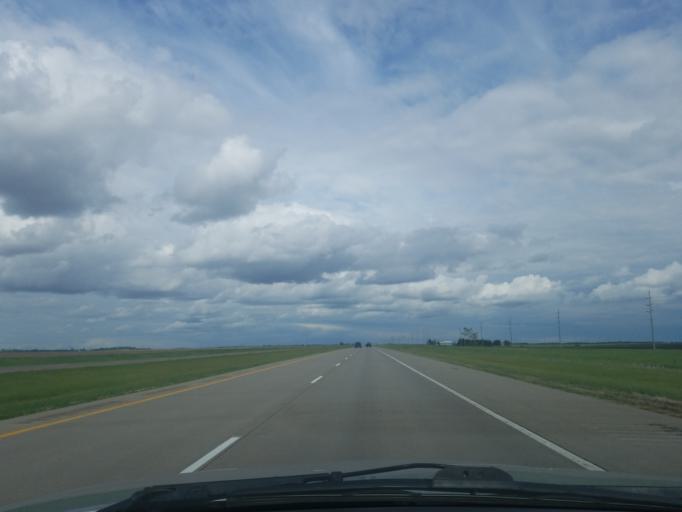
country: US
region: North Dakota
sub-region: Cass County
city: Casselton
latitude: 46.8766
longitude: -97.1572
